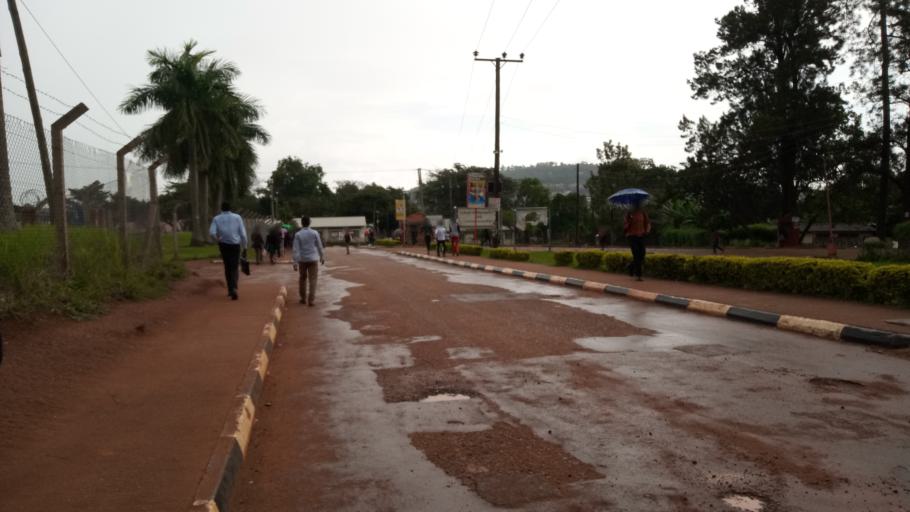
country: UG
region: Central Region
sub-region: Wakiso District
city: Kireka
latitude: 0.3462
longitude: 32.6324
